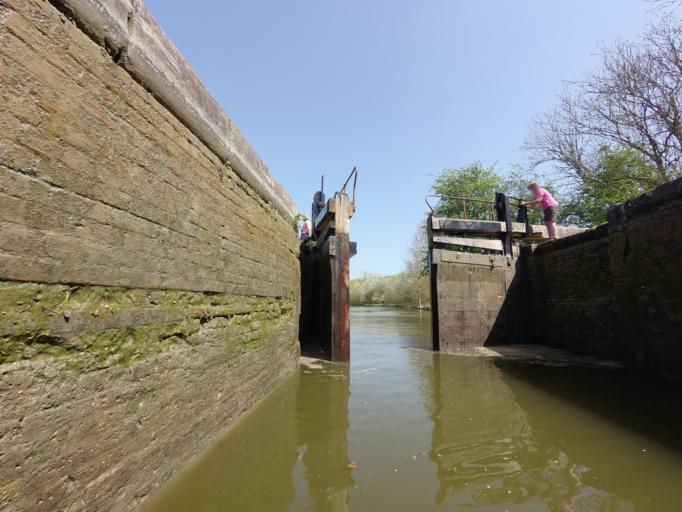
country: GB
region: England
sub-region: Buckinghamshire
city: Cheddington
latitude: 51.8410
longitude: -0.6512
